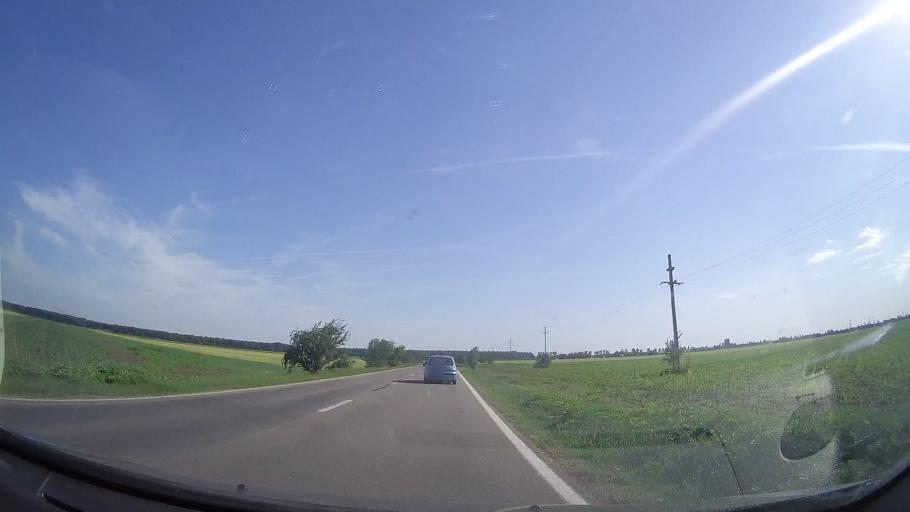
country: RO
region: Prahova
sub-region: Comuna Berceni
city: Berceni
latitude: 44.9235
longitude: 26.1023
